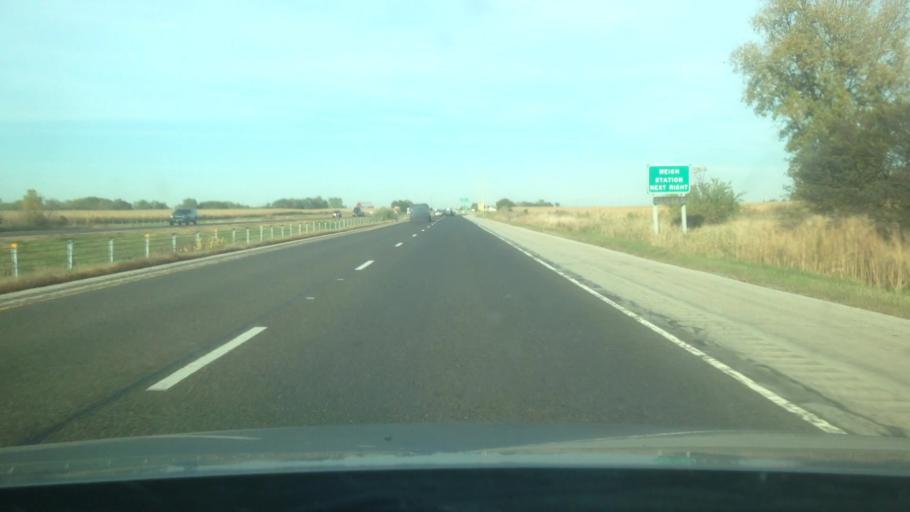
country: US
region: Illinois
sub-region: Will County
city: Peotone
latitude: 41.3549
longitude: -87.8113
